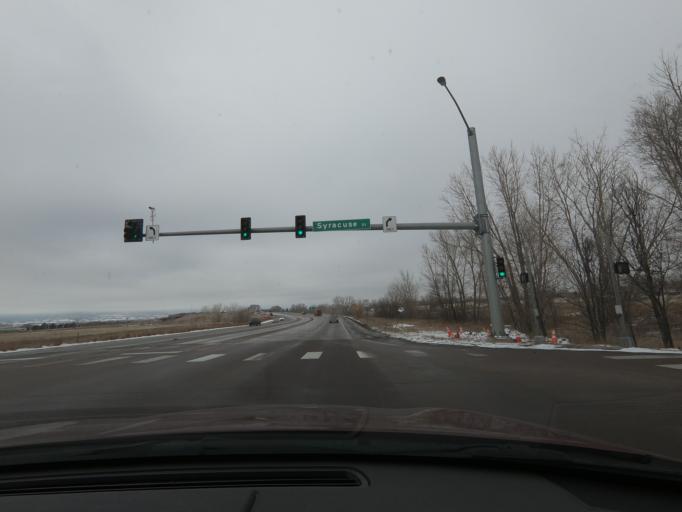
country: US
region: Colorado
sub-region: El Paso County
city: Security-Widefield
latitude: 38.7213
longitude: -104.7119
